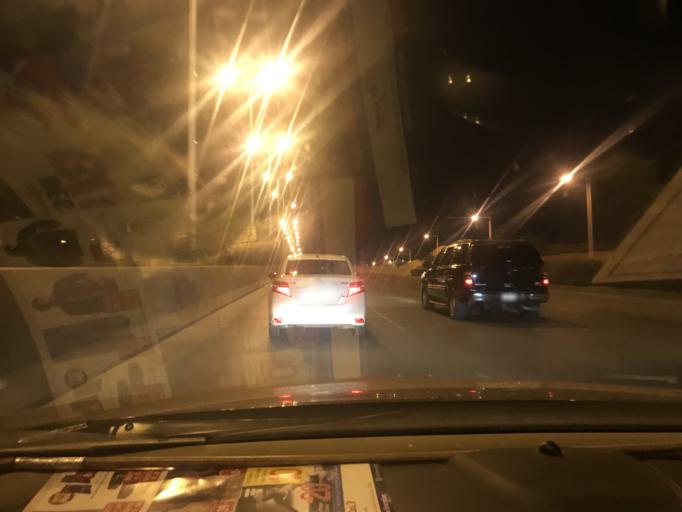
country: SA
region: Ar Riyad
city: Riyadh
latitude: 24.7360
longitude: 46.7428
